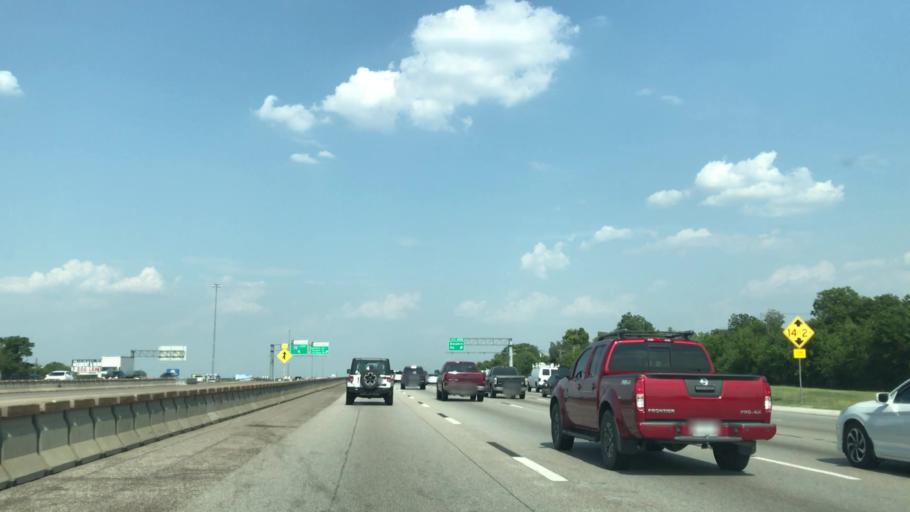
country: US
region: Texas
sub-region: Dallas County
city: Dallas
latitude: 32.7914
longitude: -96.7433
